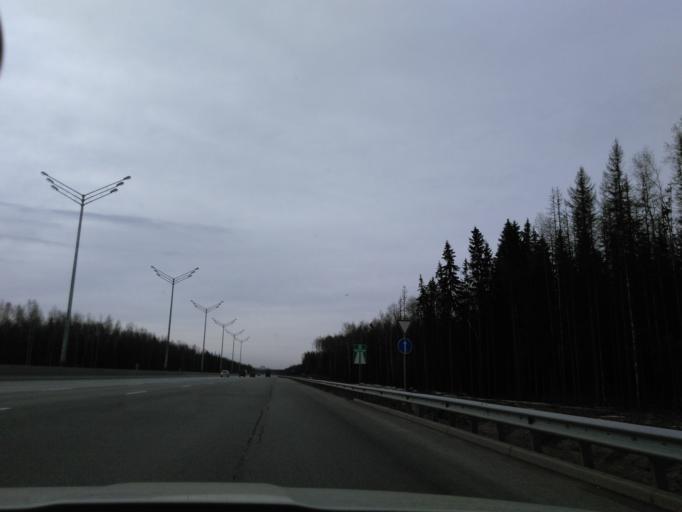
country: RU
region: Moskovskaya
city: Rzhavki
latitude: 56.0061
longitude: 37.2899
